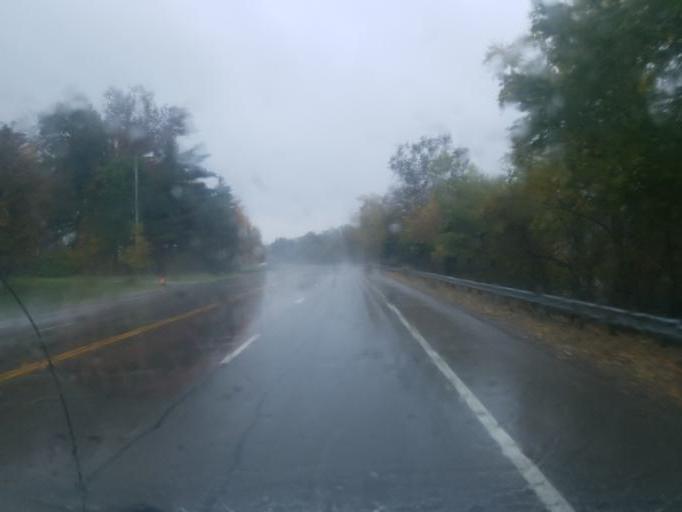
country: US
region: Ohio
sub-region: Muskingum County
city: South Zanesville
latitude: 39.8993
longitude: -81.9999
